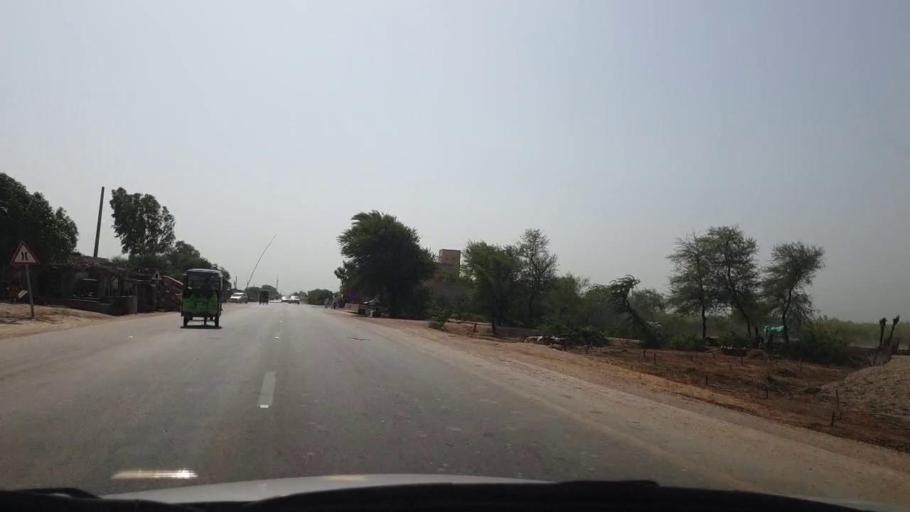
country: PK
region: Sindh
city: Tando Muhammad Khan
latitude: 25.1024
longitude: 68.5884
